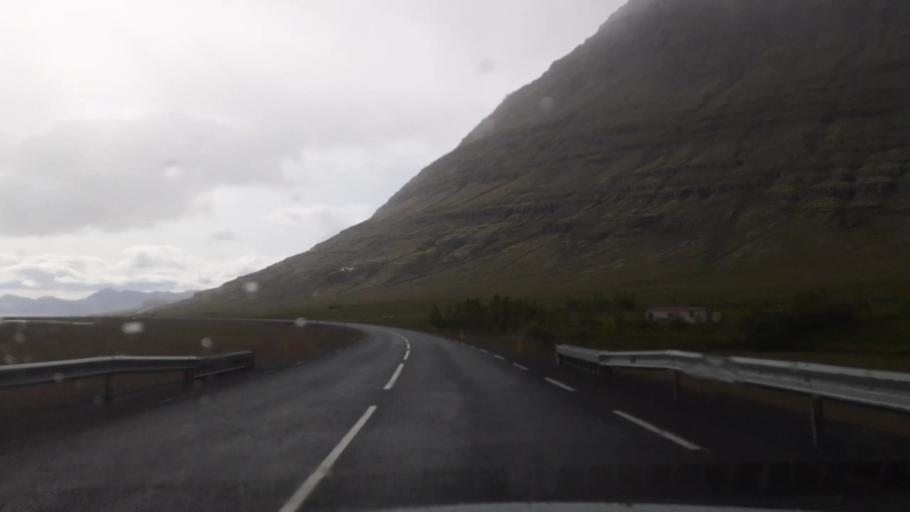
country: IS
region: East
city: Eskifjoerdur
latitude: 65.0807
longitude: -14.0536
